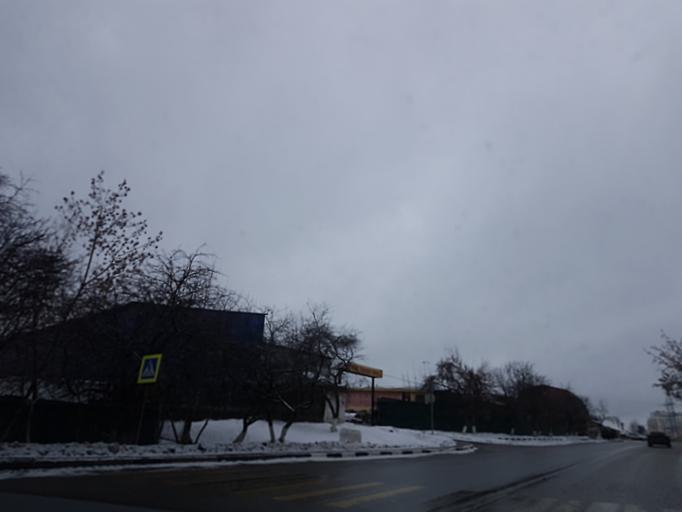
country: RU
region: Moskovskaya
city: Pavshino
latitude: 55.8226
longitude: 37.3564
